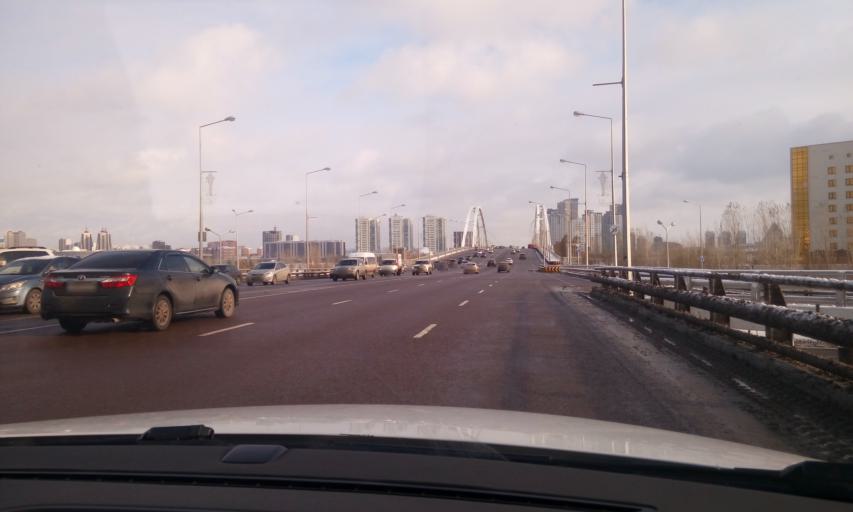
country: KZ
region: Astana Qalasy
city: Astana
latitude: 51.1322
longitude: 71.4408
